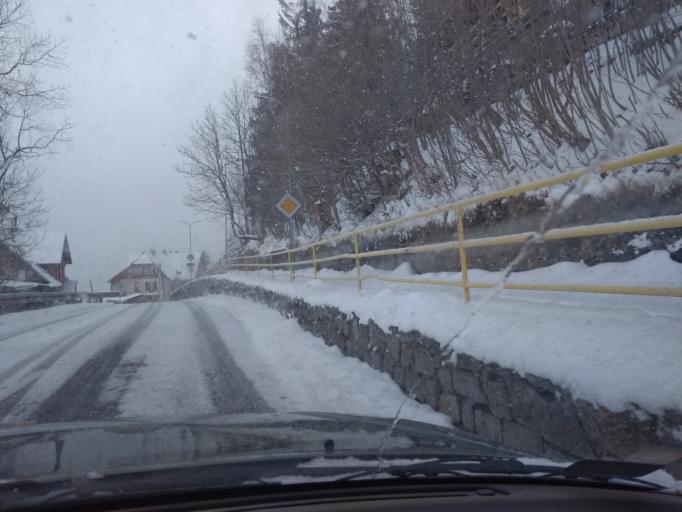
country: PL
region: Lower Silesian Voivodeship
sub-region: Powiat jeleniogorski
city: Karpacz
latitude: 50.7785
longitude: 15.7259
